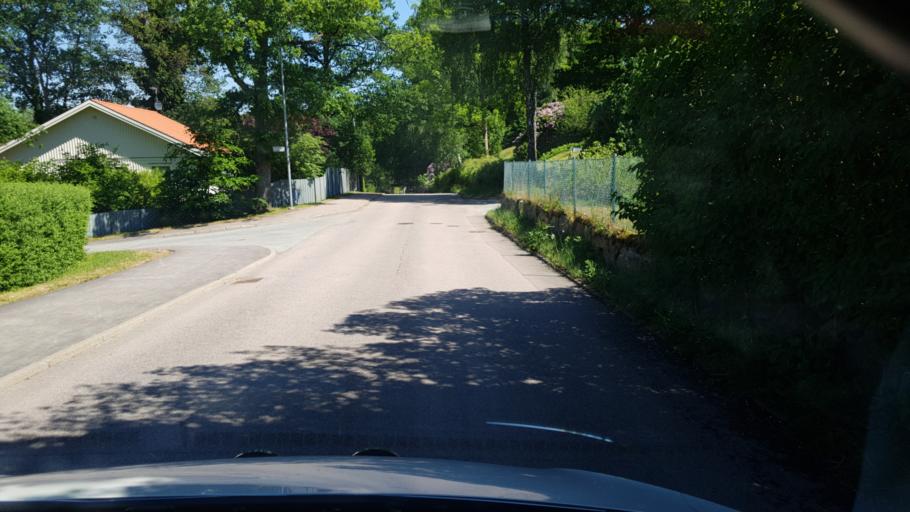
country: SE
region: Vaestra Goetaland
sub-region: Lerums Kommun
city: Stenkullen
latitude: 57.8038
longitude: 12.3611
